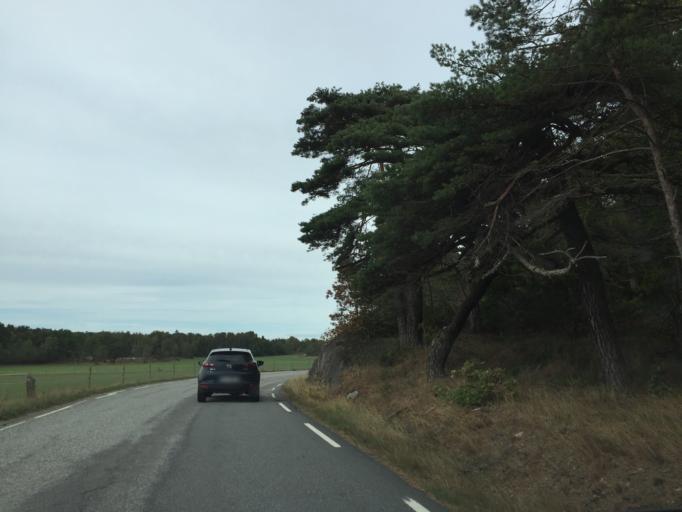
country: NO
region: Ostfold
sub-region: Hvaler
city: Skjaerhalden
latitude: 59.0343
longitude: 11.0251
